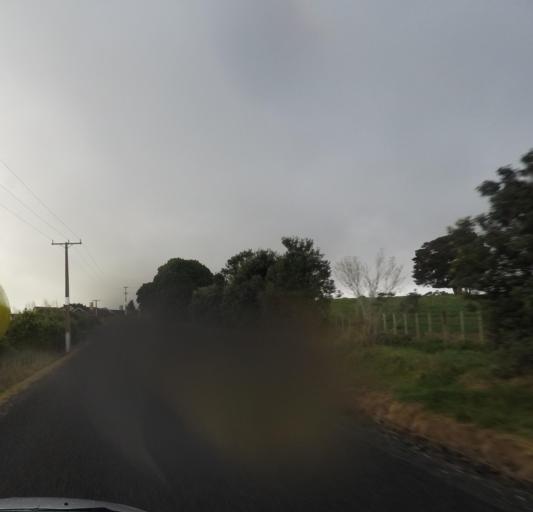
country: NZ
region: Auckland
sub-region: Auckland
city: Warkworth
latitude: -36.3768
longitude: 174.7600
